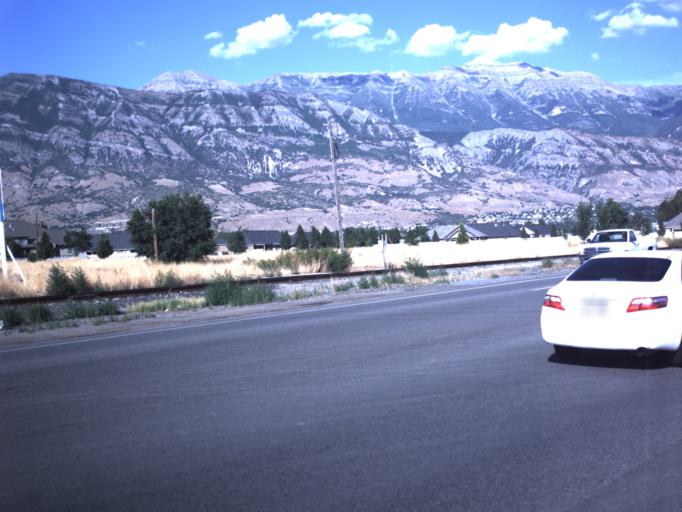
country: US
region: Utah
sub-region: Utah County
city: American Fork
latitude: 40.3713
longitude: -111.7746
